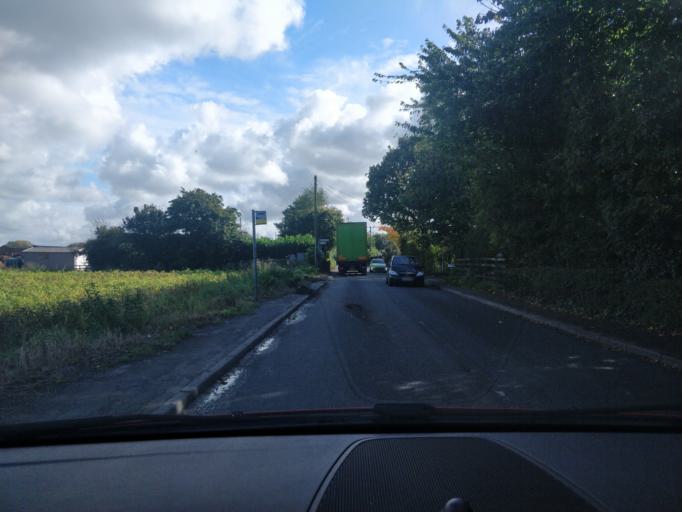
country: GB
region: England
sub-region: Lancashire
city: Ormskirk
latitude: 53.5983
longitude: -2.9000
